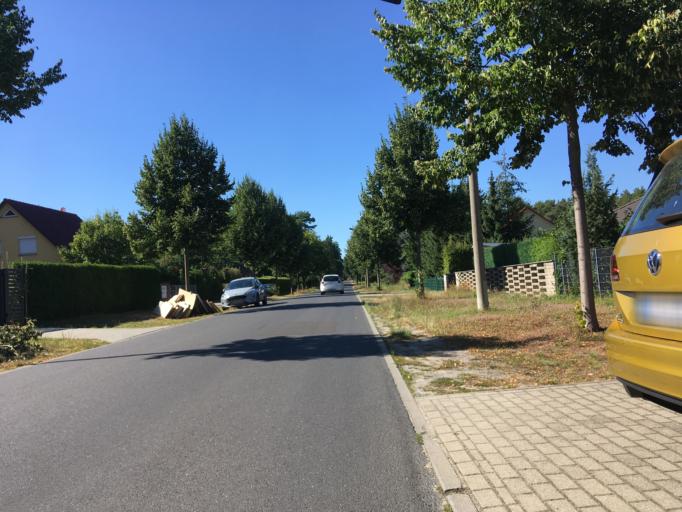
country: DE
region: Brandenburg
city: Schulzendorf
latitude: 52.3492
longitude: 13.5981
